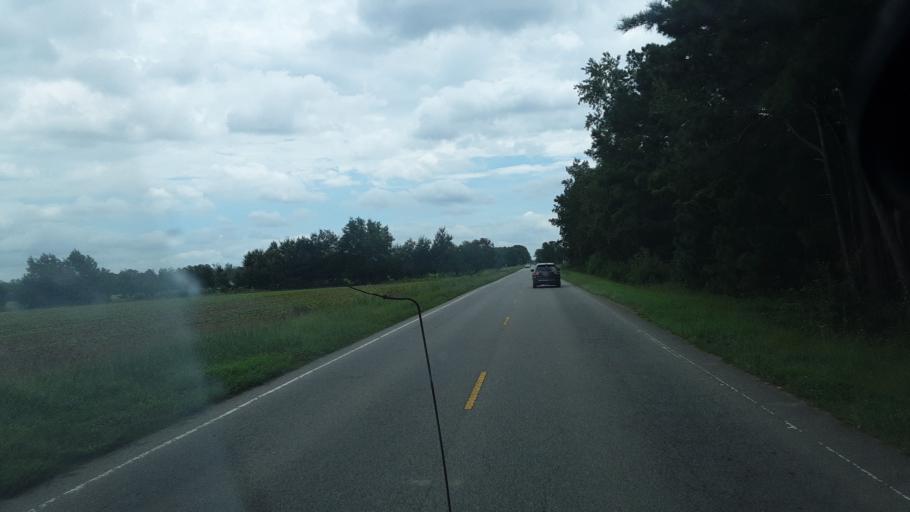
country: US
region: North Carolina
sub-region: Robeson County
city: Maxton
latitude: 34.6723
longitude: -79.4098
